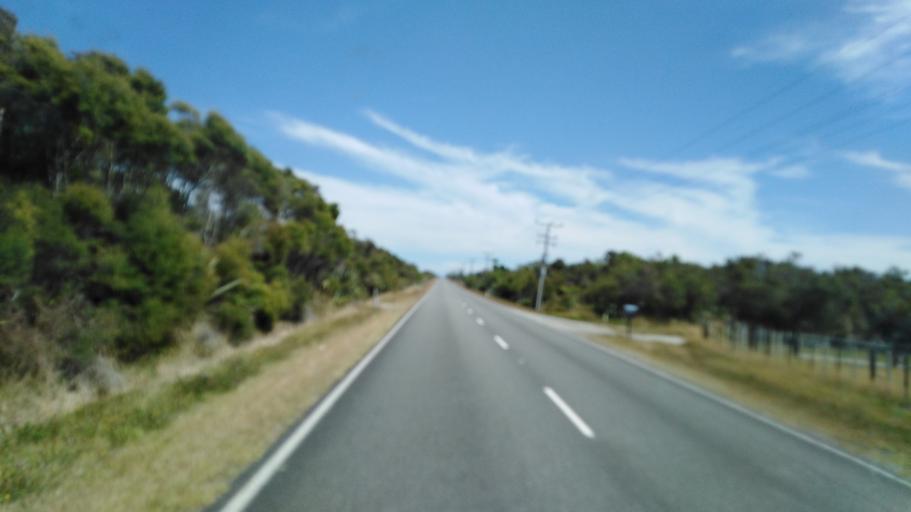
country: NZ
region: West Coast
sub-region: Buller District
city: Westport
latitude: -41.7459
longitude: 171.6842
